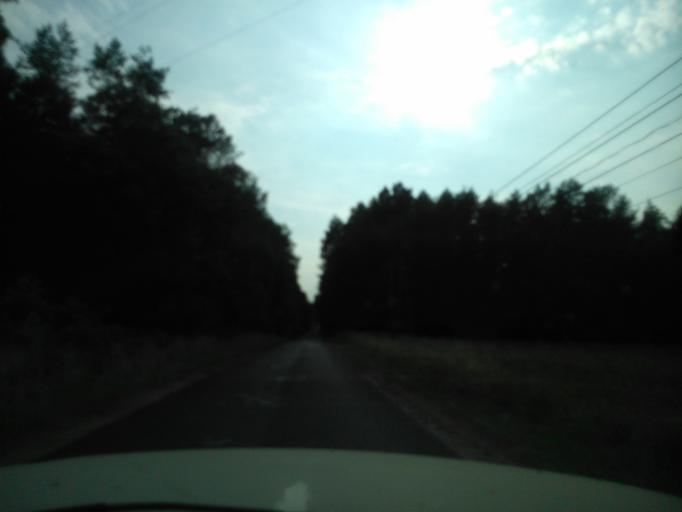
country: PL
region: Kujawsko-Pomorskie
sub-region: Powiat golubsko-dobrzynski
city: Radomin
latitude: 53.1469
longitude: 19.1324
